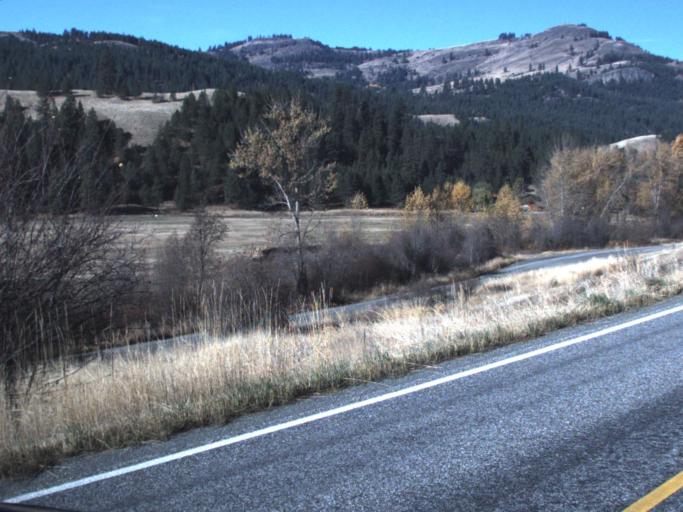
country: US
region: Washington
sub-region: Ferry County
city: Republic
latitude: 48.8360
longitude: -118.5925
